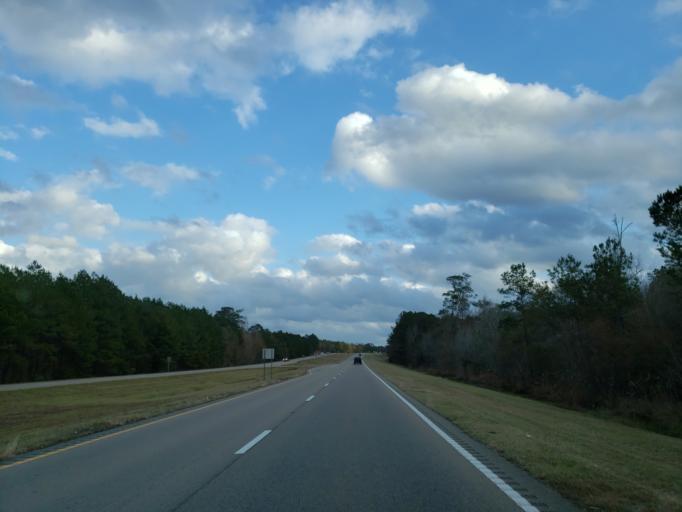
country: US
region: Mississippi
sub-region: Perry County
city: New Augusta
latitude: 31.1877
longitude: -88.9642
